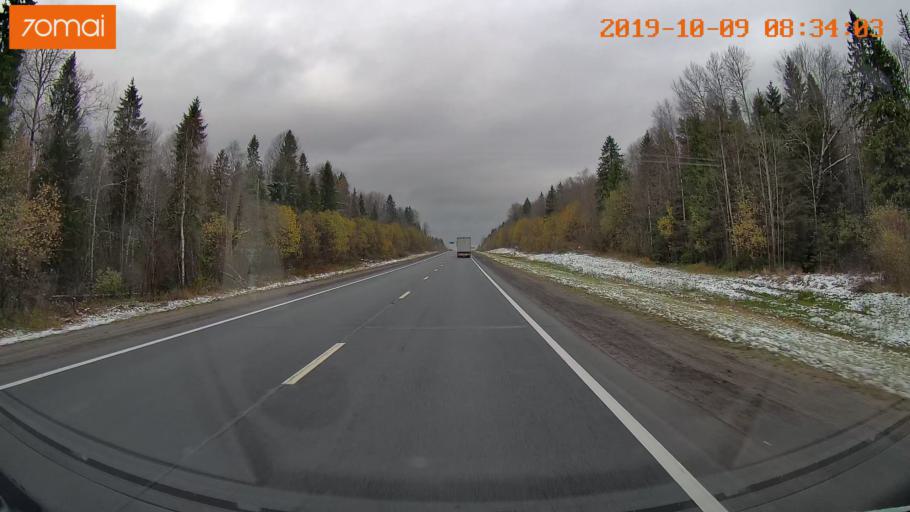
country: RU
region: Vologda
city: Gryazovets
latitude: 58.8913
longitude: 40.1881
